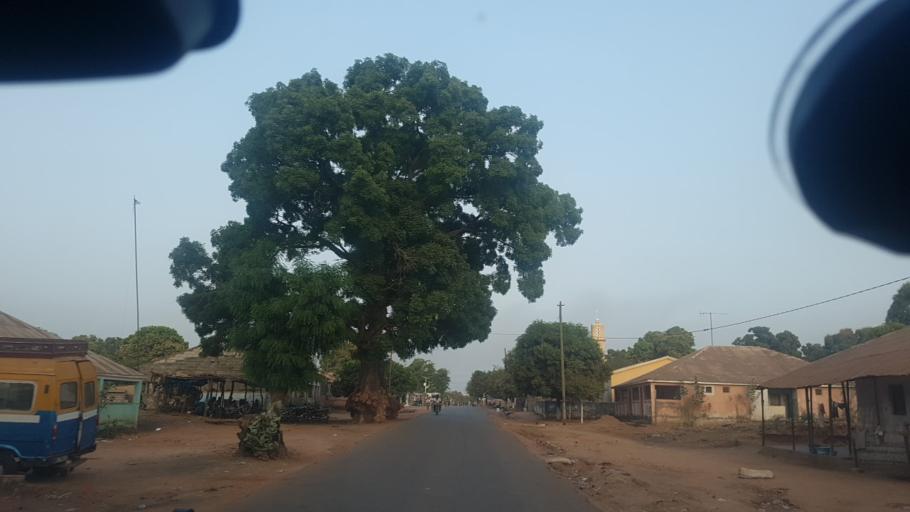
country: SN
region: Ziguinchor
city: Adeane
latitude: 12.4099
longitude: -15.8026
